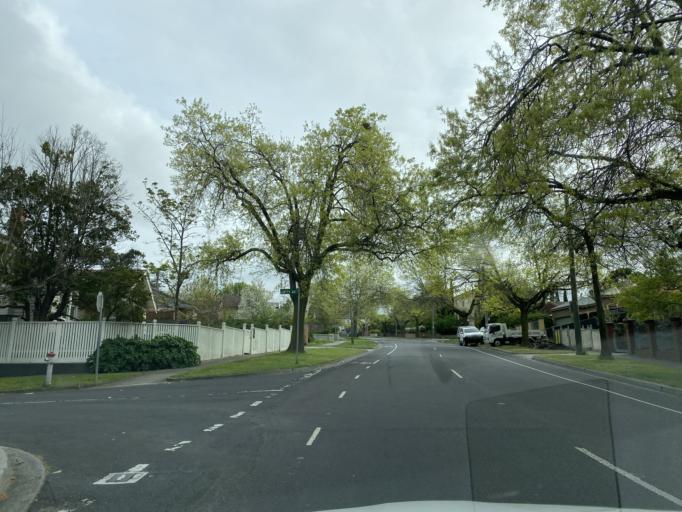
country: AU
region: Victoria
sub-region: Boroondara
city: Camberwell
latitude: -37.8419
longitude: 145.0833
